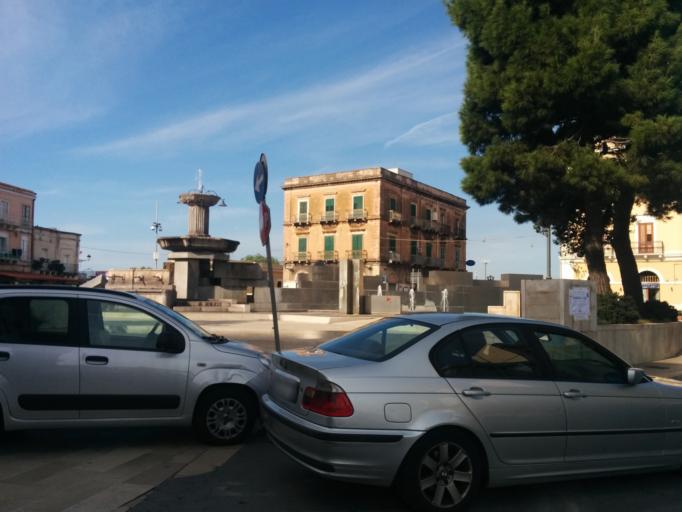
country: IT
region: Apulia
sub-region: Provincia di Taranto
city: Statte
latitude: 40.4790
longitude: 17.2278
